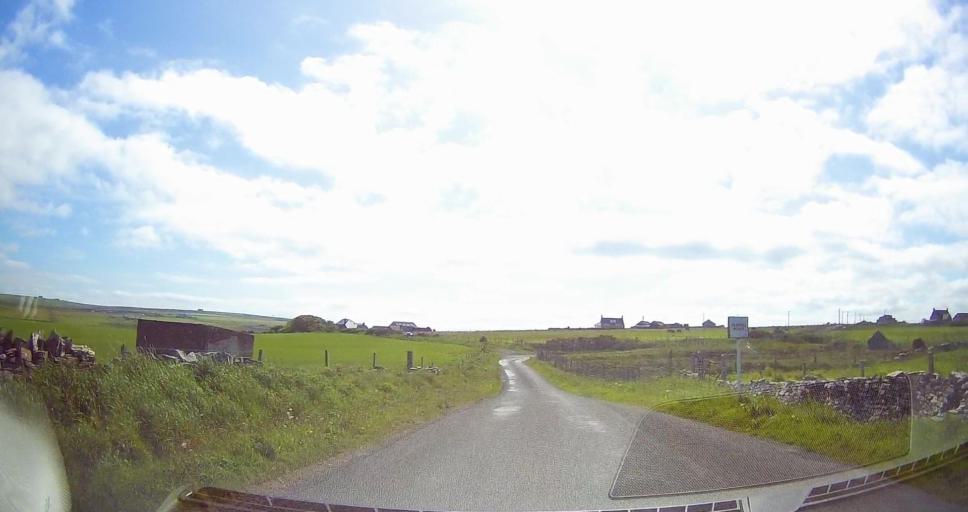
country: GB
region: Scotland
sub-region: Orkney Islands
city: Kirkwall
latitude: 58.9632
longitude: -2.9441
